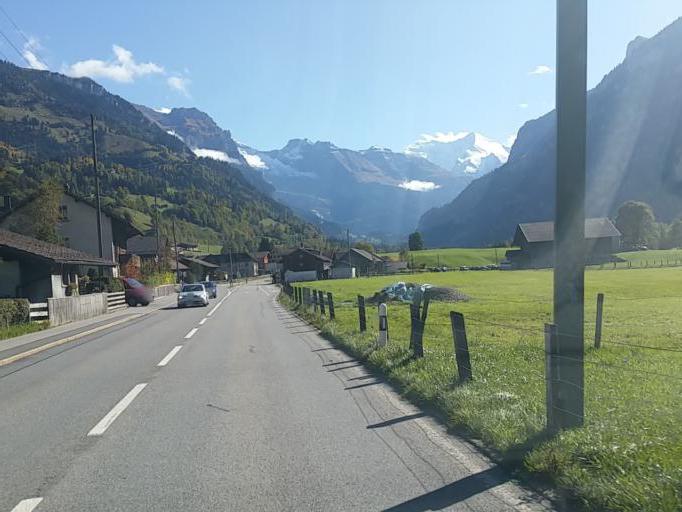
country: CH
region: Bern
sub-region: Frutigen-Niedersimmental District
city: Frutigen
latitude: 46.5675
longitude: 7.6560
